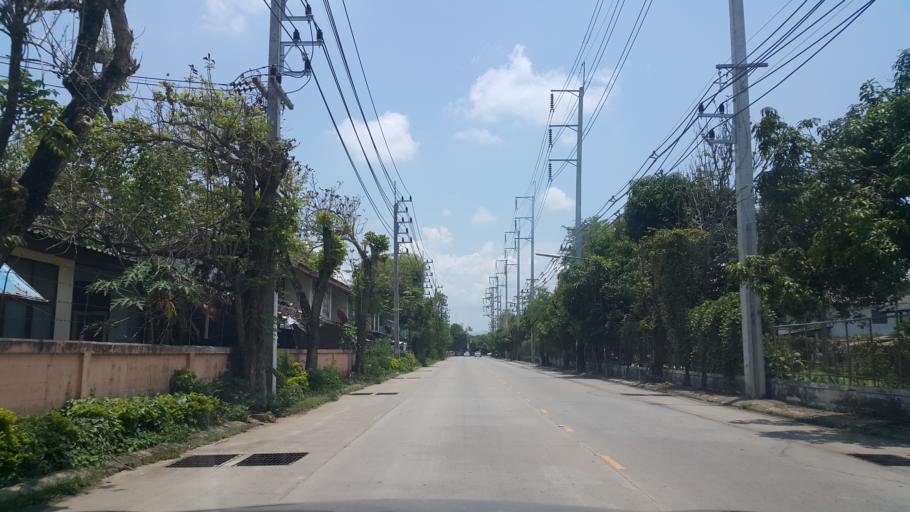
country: TH
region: Chiang Rai
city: Chiang Rai
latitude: 19.9104
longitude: 99.8220
